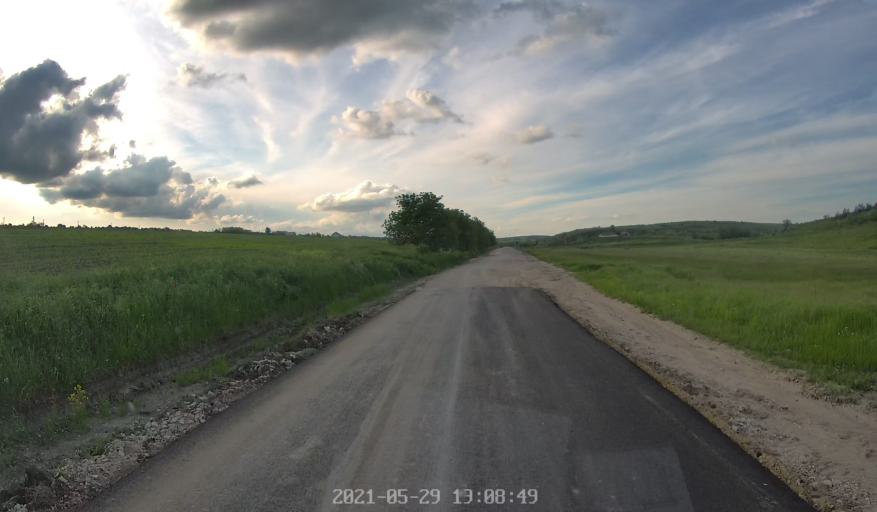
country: MD
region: Chisinau
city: Singera
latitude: 46.8298
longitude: 28.9564
